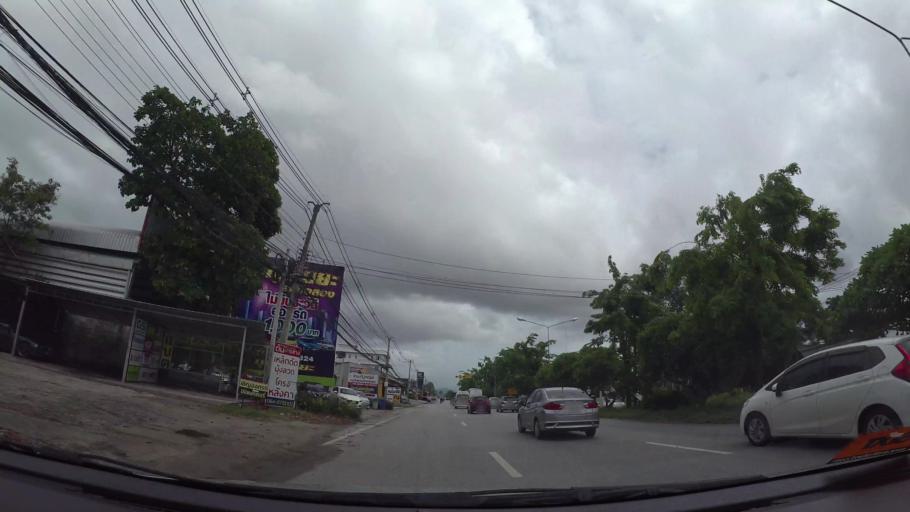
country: TH
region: Rayong
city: Rayong
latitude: 12.6846
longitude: 101.2165
